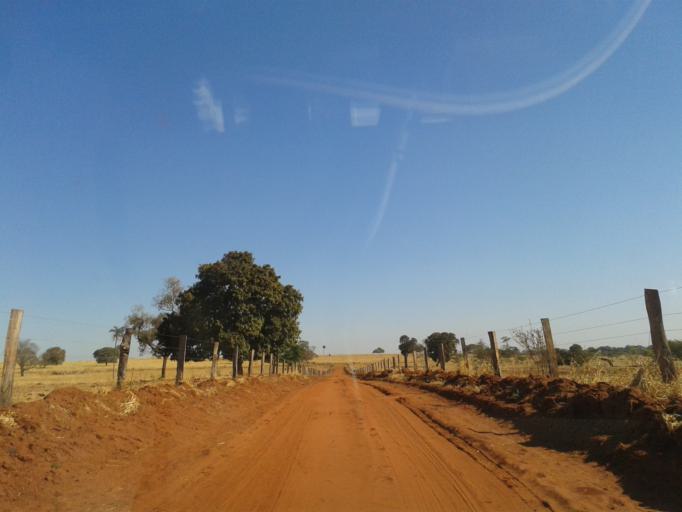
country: BR
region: Minas Gerais
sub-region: Santa Vitoria
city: Santa Vitoria
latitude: -19.0504
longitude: -49.9359
